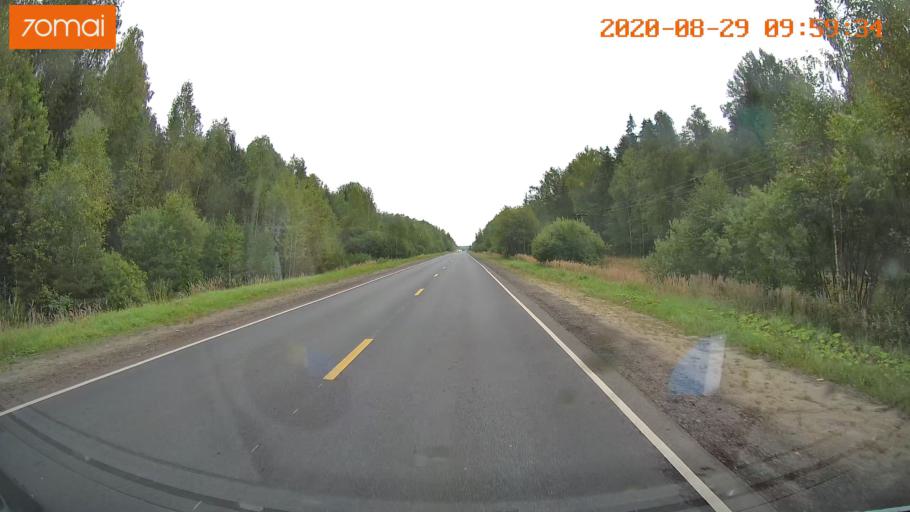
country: RU
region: Ivanovo
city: Zarechnyy
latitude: 57.4109
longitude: 42.3696
